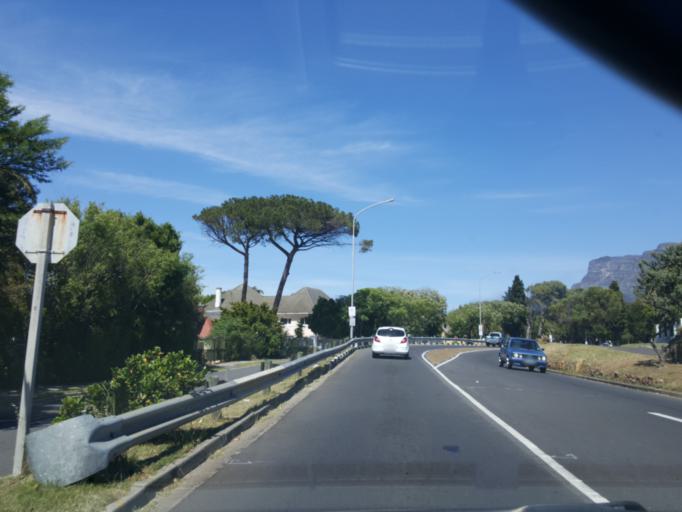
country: ZA
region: Western Cape
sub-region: City of Cape Town
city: Rosebank
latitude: -33.9416
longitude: 18.4998
